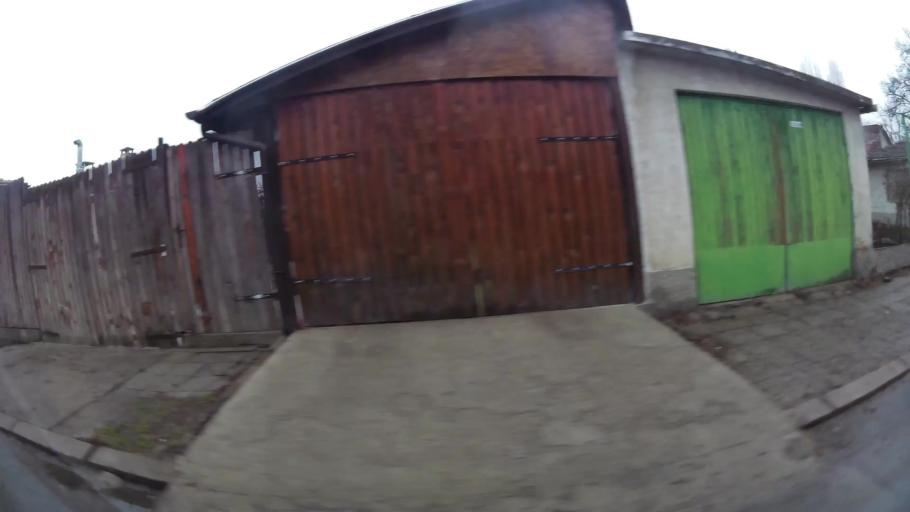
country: BG
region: Sofia-Capital
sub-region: Stolichna Obshtina
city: Sofia
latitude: 42.7322
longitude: 23.2989
